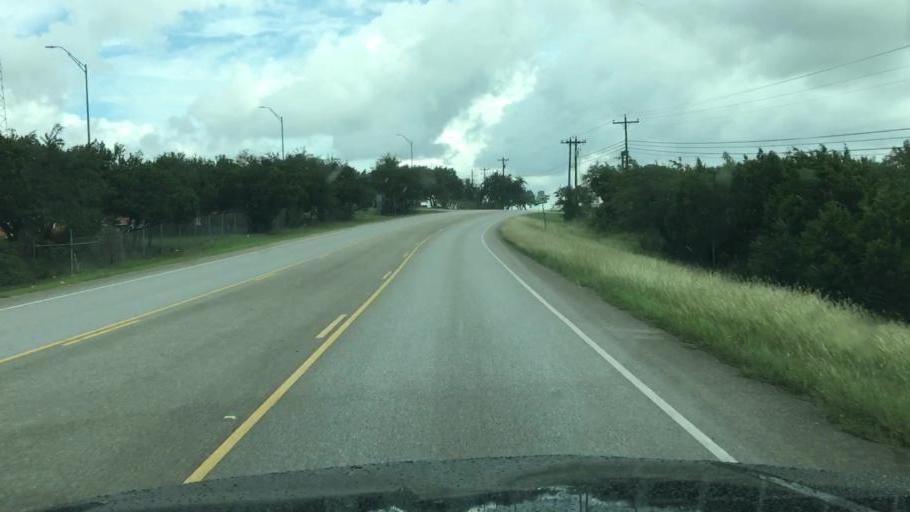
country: US
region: Texas
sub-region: Travis County
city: Bee Cave
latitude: 30.2058
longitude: -97.9727
